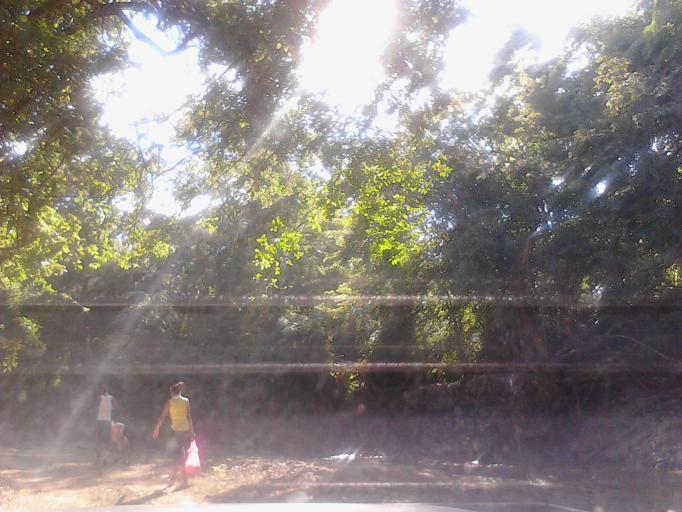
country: NI
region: Rivas
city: Tola
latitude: 11.5003
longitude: -86.0499
